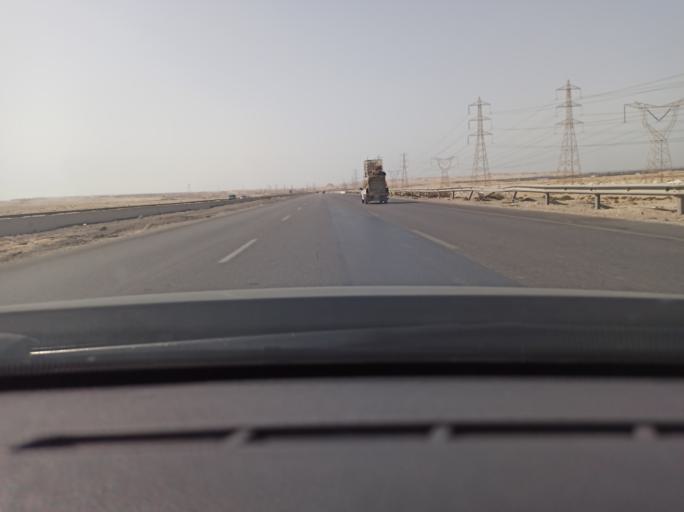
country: EG
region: Muhafazat al Qahirah
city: Halwan
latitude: 29.7351
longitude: 31.4078
